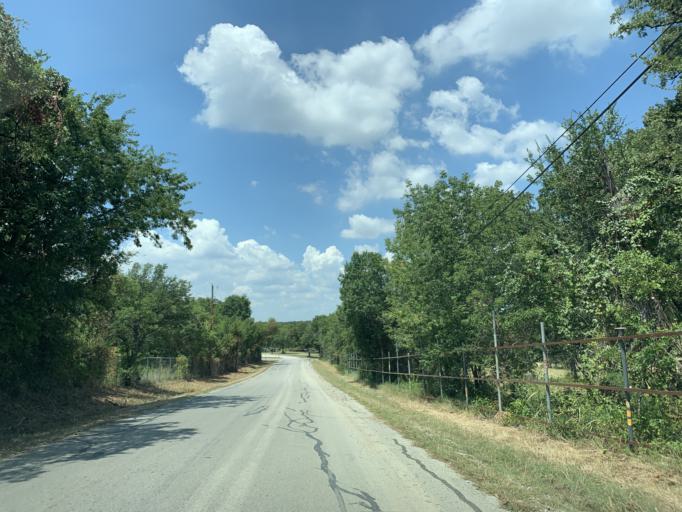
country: US
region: Texas
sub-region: Tarrant County
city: Lakeside
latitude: 32.8417
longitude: -97.5011
